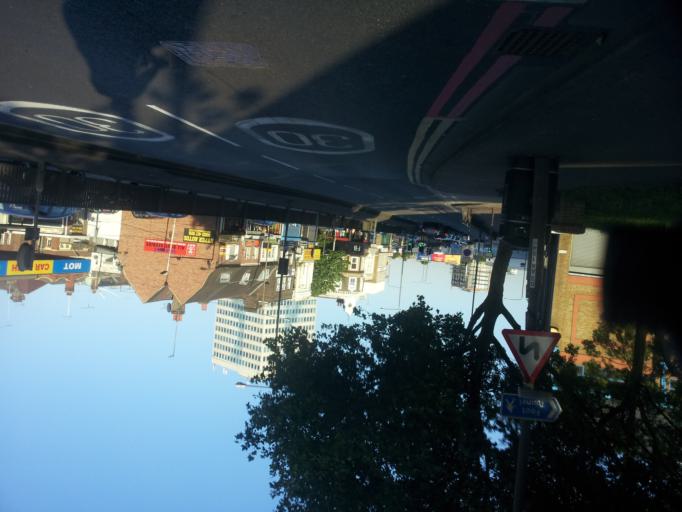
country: GB
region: England
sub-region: Greater London
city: Woolwich
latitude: 51.4936
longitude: 0.0620
